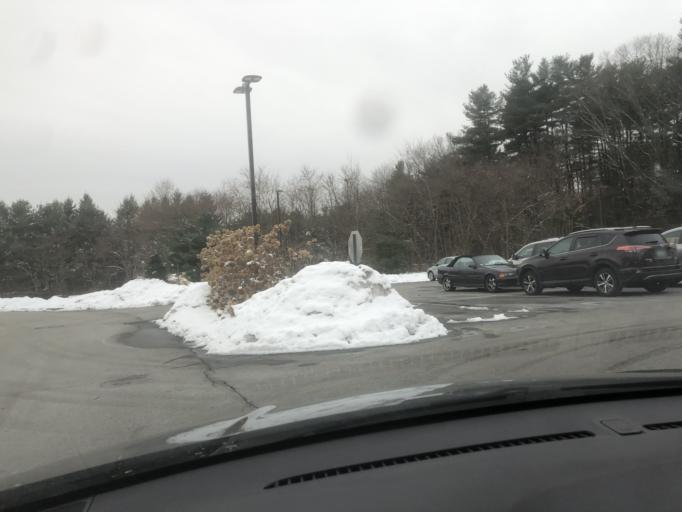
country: US
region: Massachusetts
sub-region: Middlesex County
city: Tewksbury
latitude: 42.5973
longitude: -71.2194
